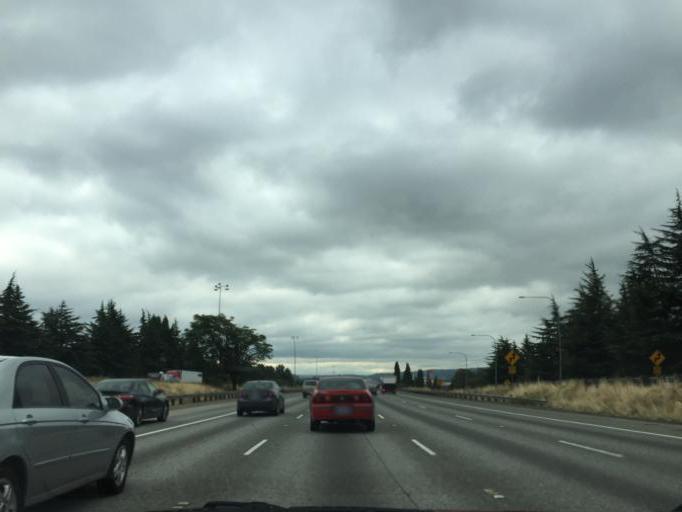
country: US
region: Washington
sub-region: King County
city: Seattle
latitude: 47.5557
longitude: -122.3197
